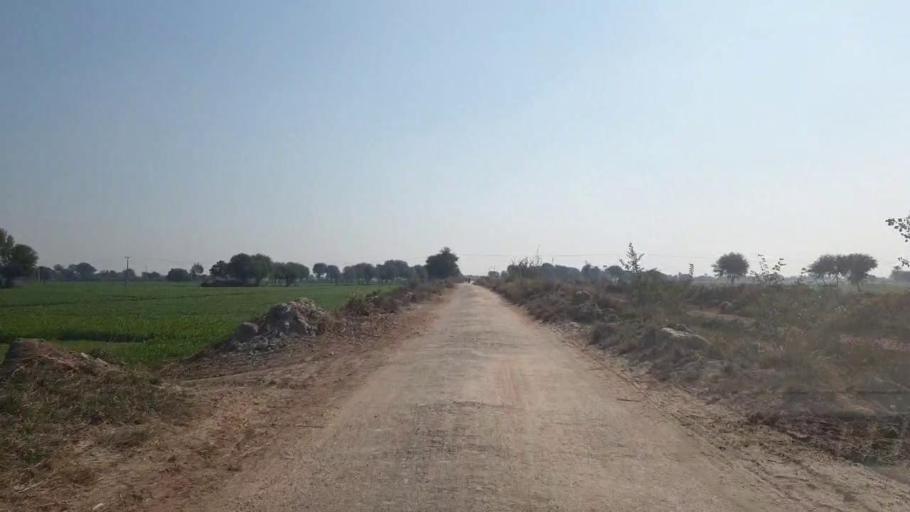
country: PK
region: Sindh
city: Shahdadpur
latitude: 25.9589
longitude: 68.6245
